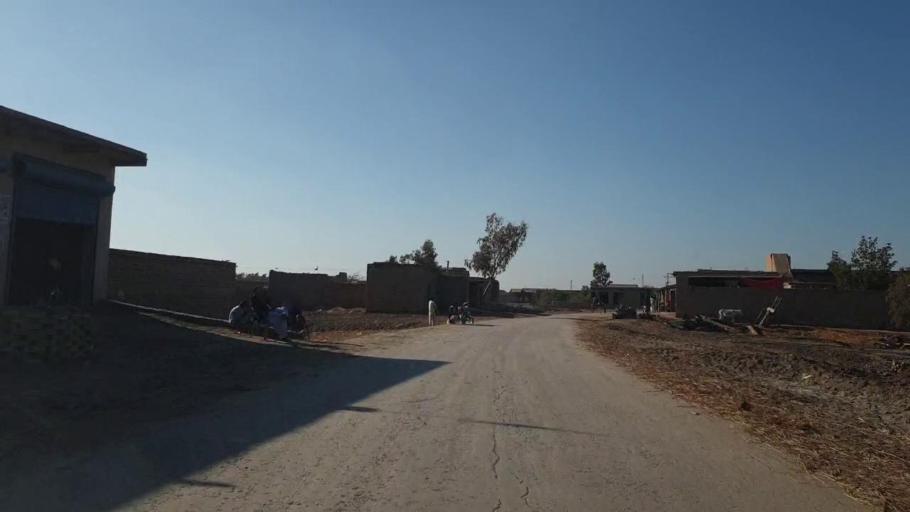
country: PK
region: Sindh
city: New Badah
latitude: 27.3248
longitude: 68.0327
